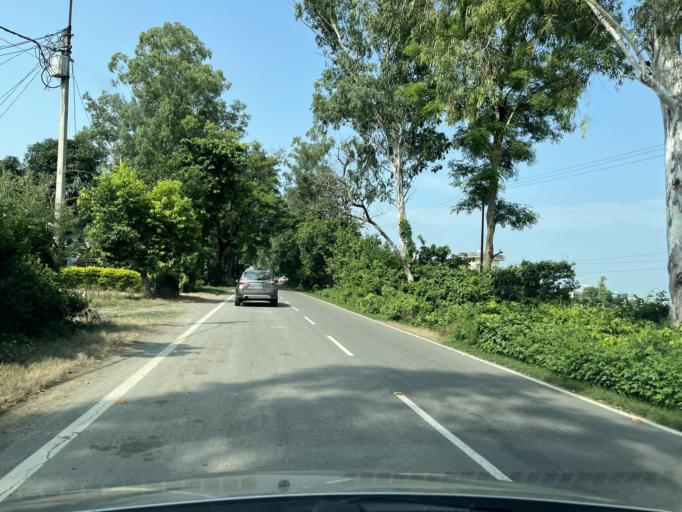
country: IN
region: Uttarakhand
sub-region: Udham Singh Nagar
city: Bazpur
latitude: 29.2132
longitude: 79.2210
